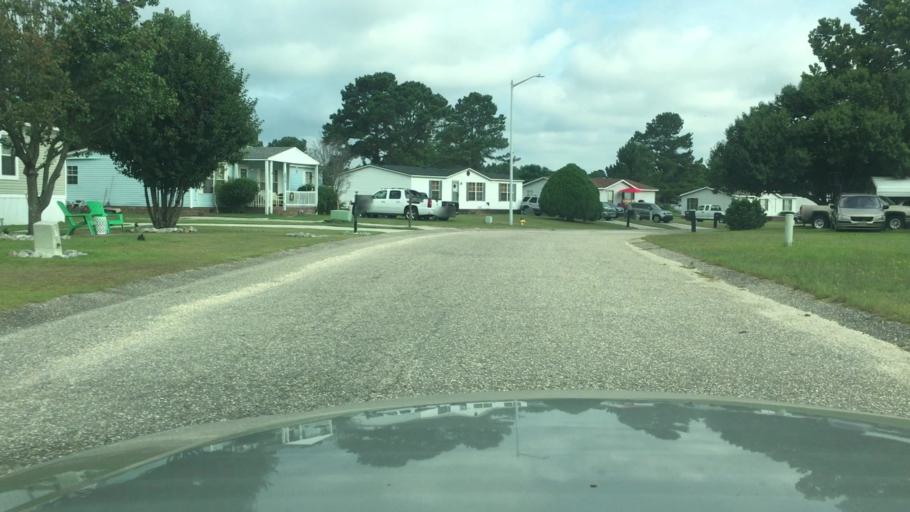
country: US
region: North Carolina
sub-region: Cumberland County
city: Hope Mills
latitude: 34.9481
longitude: -78.8747
